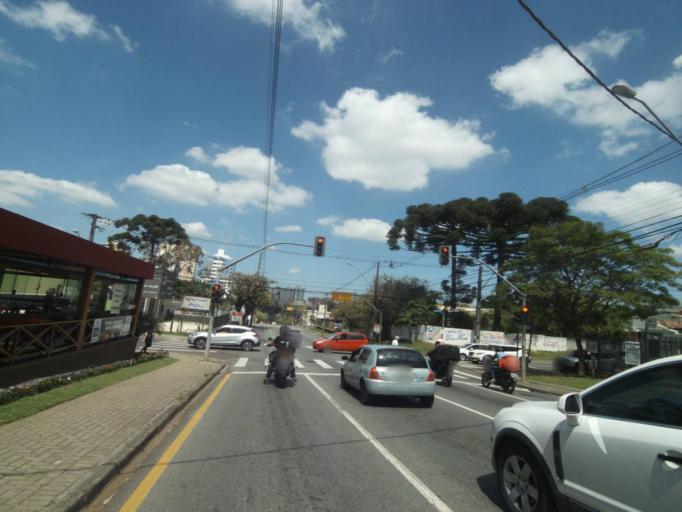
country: BR
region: Parana
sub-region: Curitiba
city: Curitiba
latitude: -25.3996
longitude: -49.2475
